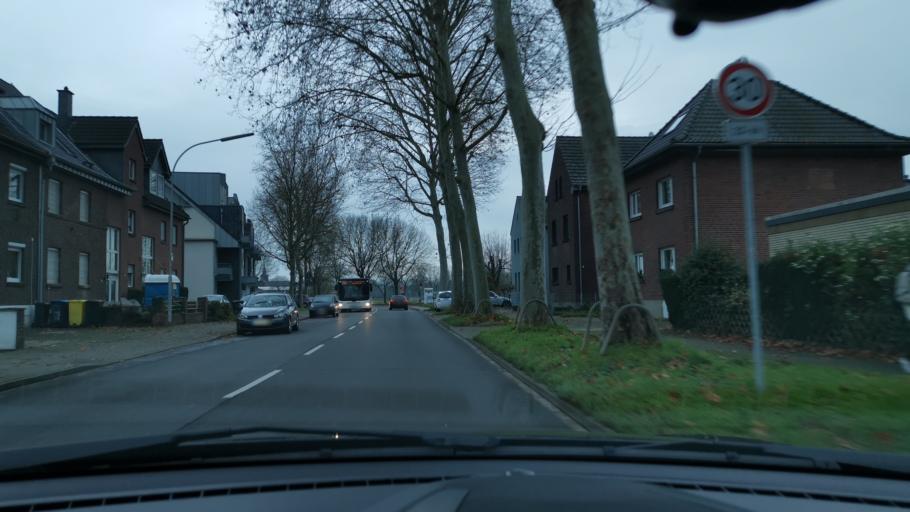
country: DE
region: North Rhine-Westphalia
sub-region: Regierungsbezirk Dusseldorf
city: Neubrueck
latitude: 51.1167
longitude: 6.6250
